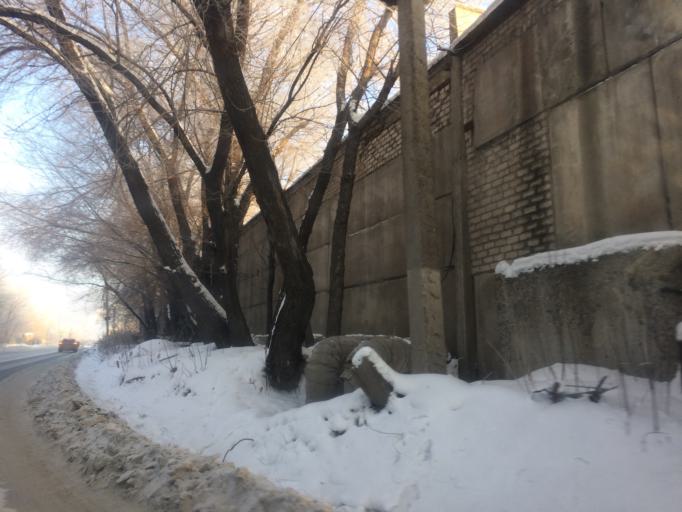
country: RU
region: Chelyabinsk
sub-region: Gorod Magnitogorsk
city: Magnitogorsk
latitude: 53.3938
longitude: 59.0709
